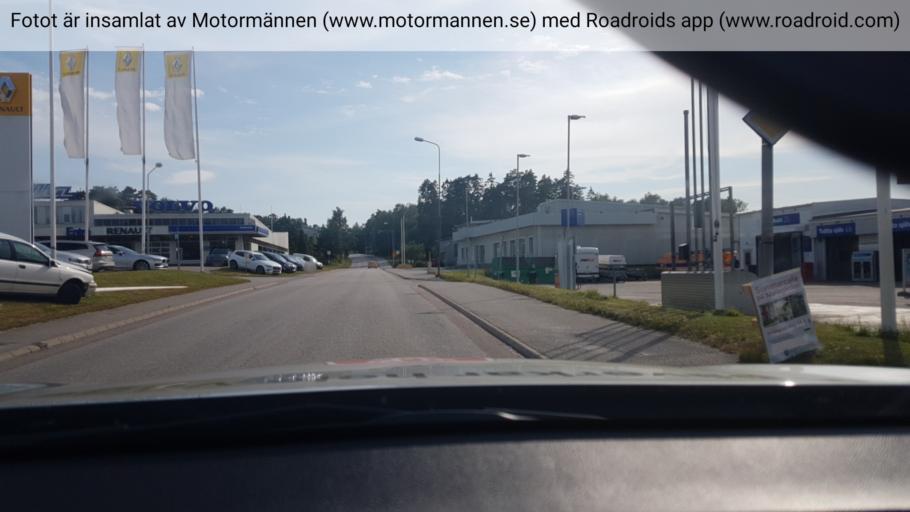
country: SE
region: Vaestra Goetaland
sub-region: Stenungsunds Kommun
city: Stenungsund
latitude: 58.0750
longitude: 11.8401
